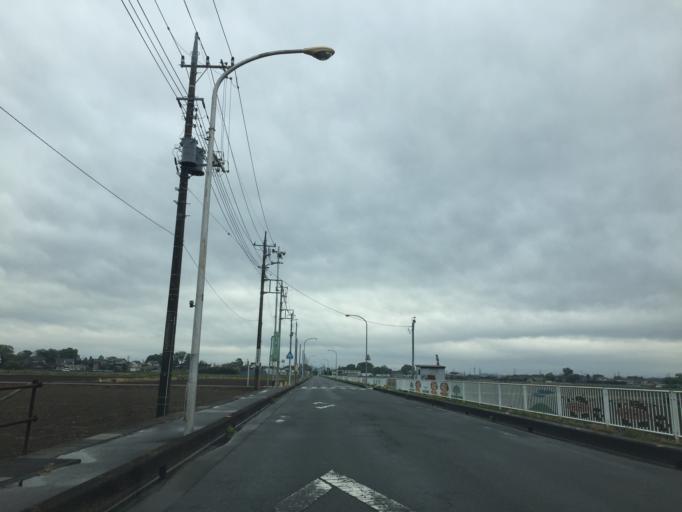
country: JP
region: Saitama
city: Shiki
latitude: 35.8690
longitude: 139.5656
